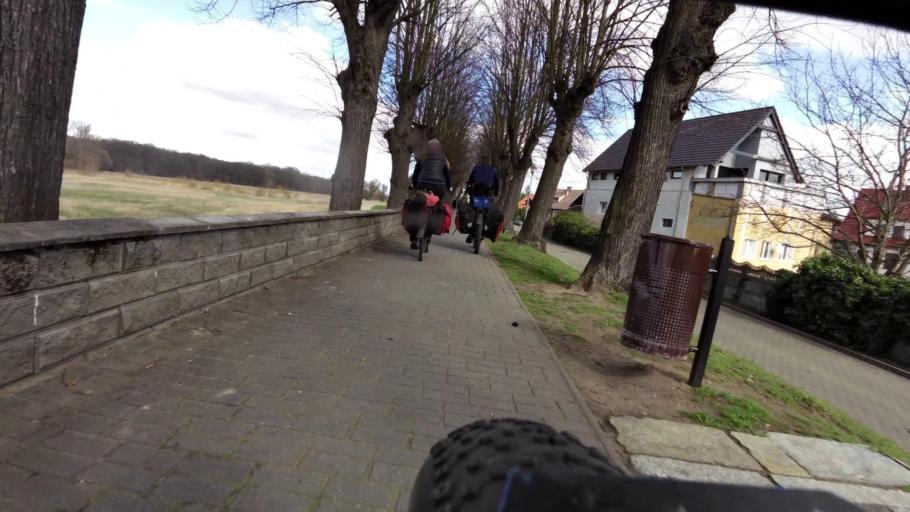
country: PL
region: Lubusz
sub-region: Powiat slubicki
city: Slubice
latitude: 52.3570
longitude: 14.5580
